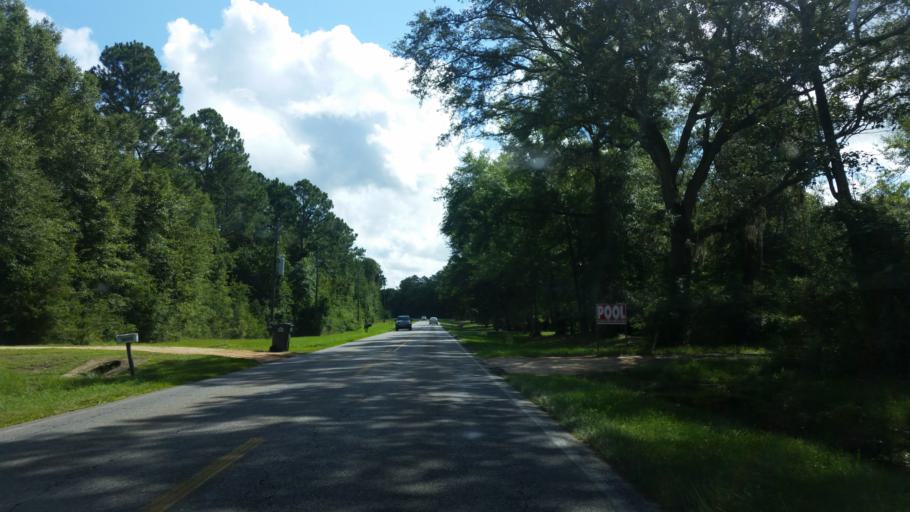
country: US
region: Florida
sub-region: Santa Rosa County
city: Milton
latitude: 30.6414
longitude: -87.0211
